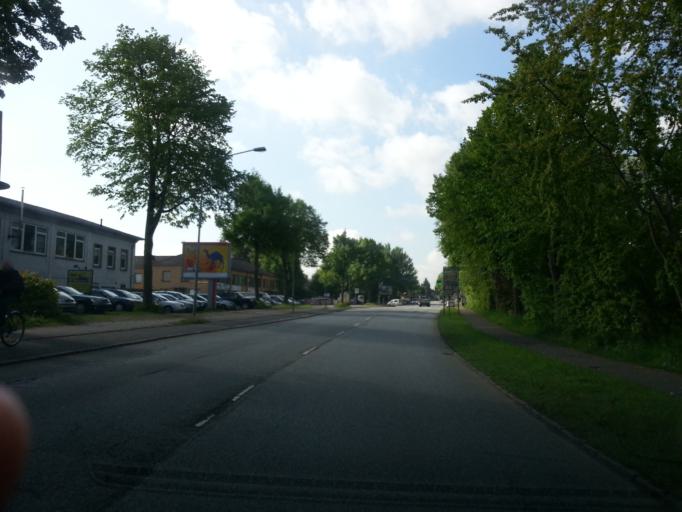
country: DE
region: Schleswig-Holstein
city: Bad Schwartau
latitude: 53.8999
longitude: 10.6898
